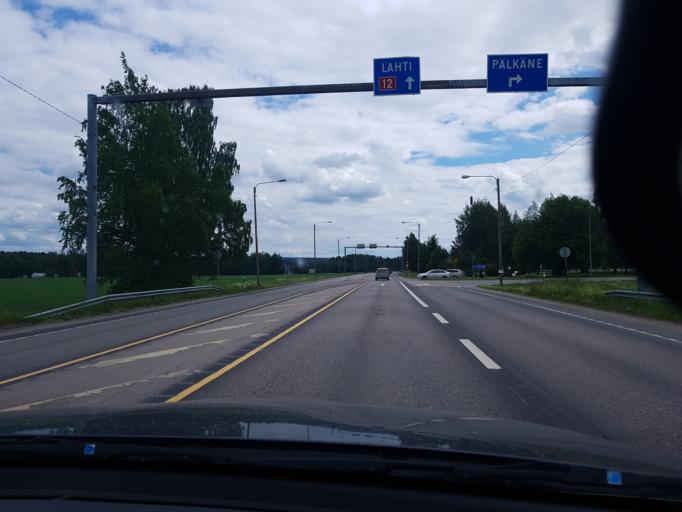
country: FI
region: Pirkanmaa
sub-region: Tampere
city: Paelkaene
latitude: 61.3414
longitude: 24.2704
